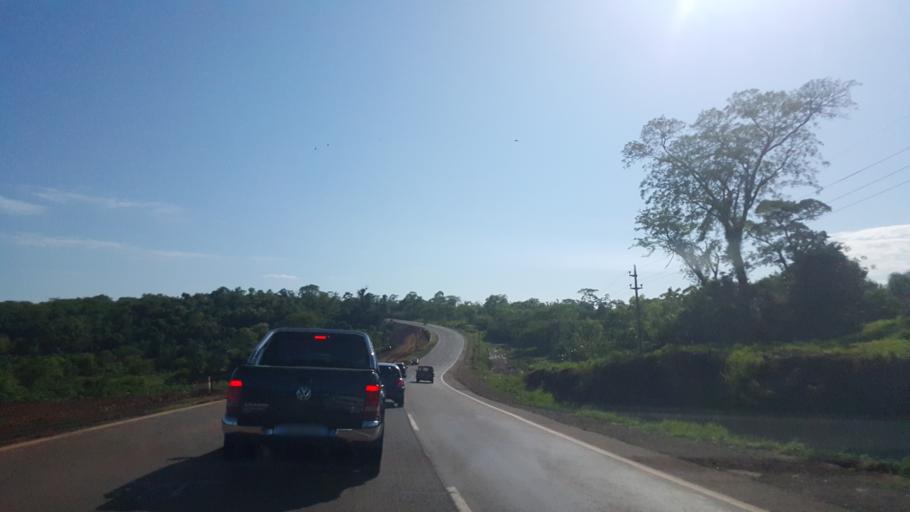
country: AR
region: Misiones
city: Santa Ana
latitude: -27.3545
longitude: -55.5532
